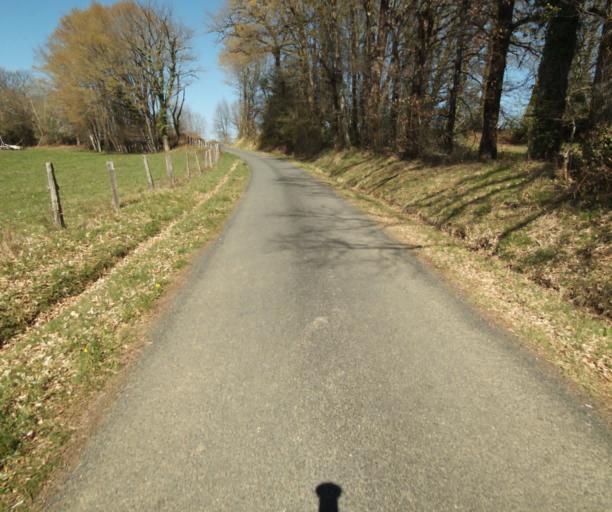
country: FR
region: Limousin
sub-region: Departement de la Correze
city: Saint-Clement
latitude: 45.3243
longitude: 1.6932
